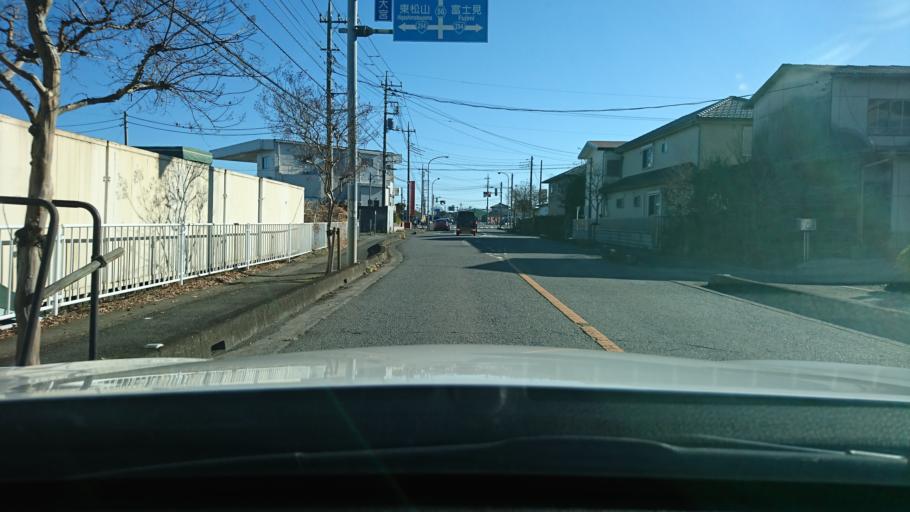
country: JP
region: Saitama
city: Kamifukuoka
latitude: 35.8827
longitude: 139.5326
